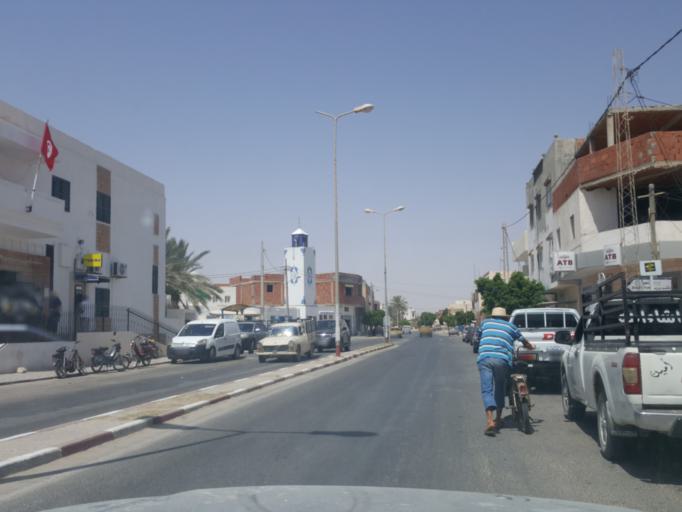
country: TN
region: Qabis
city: Gabes
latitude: 33.9607
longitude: 9.9967
